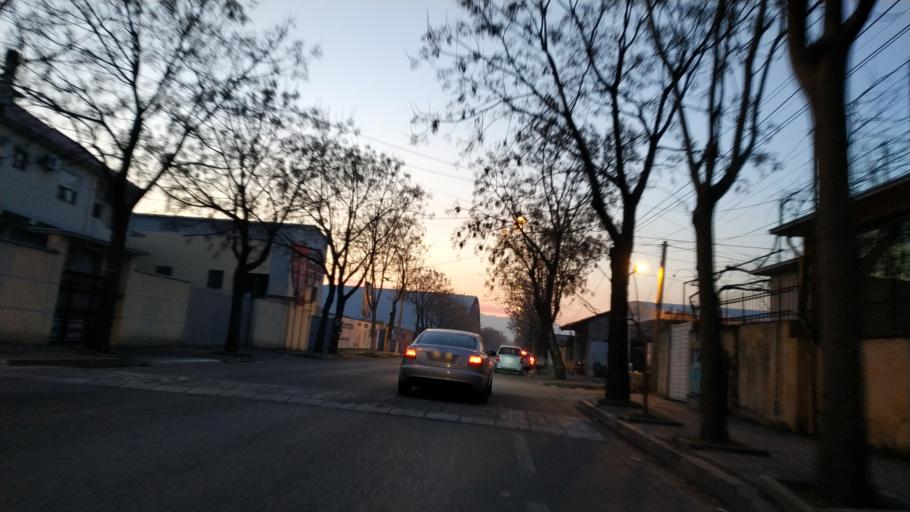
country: AL
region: Shkoder
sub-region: Rrethi i Shkodres
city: Shkoder
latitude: 42.0779
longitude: 19.5102
